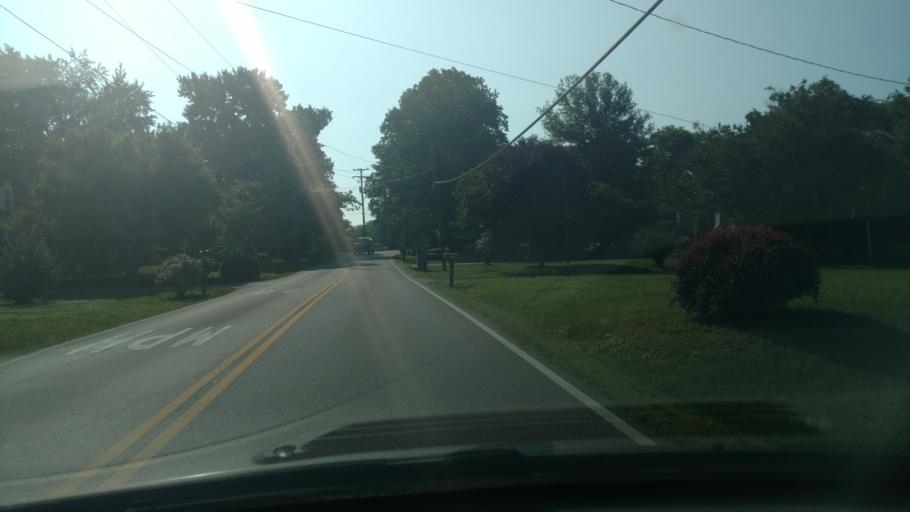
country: US
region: Tennessee
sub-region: Davidson County
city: Nashville
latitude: 36.2228
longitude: -86.7205
